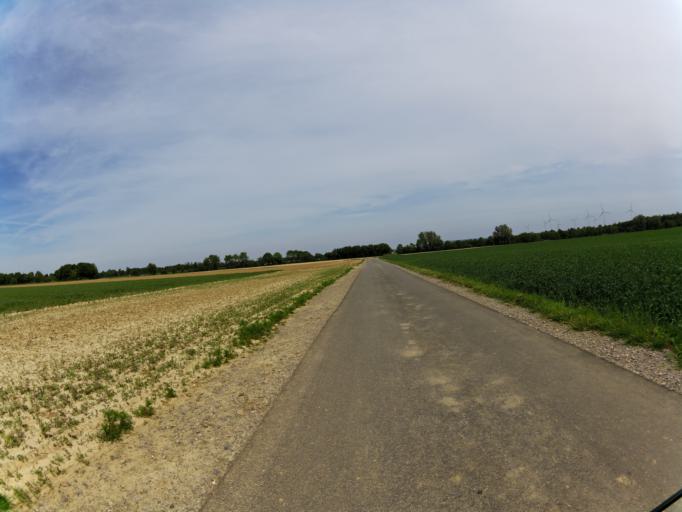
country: DE
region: North Rhine-Westphalia
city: Niedermerz
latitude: 50.8755
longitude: 6.2469
